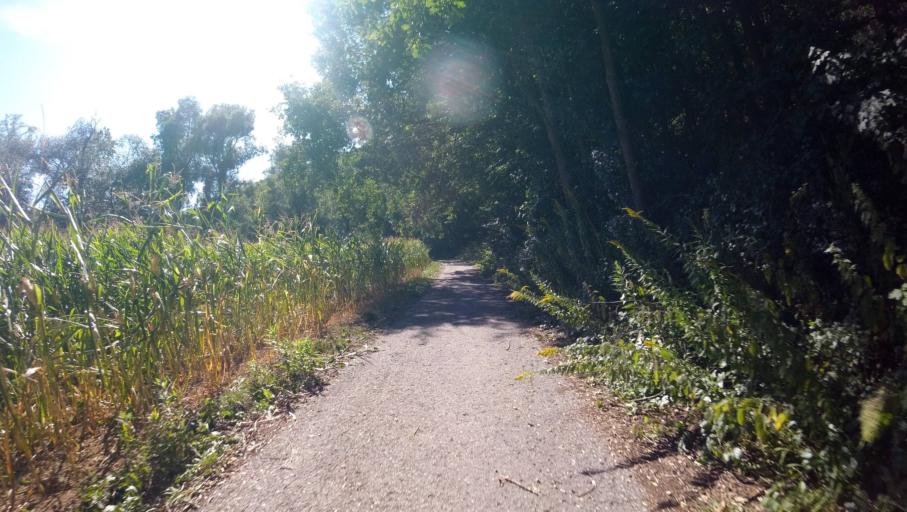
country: DE
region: Baden-Wuerttemberg
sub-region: Regierungsbezirk Stuttgart
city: Kirchberg an der Murr
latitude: 48.9342
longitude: 9.3507
